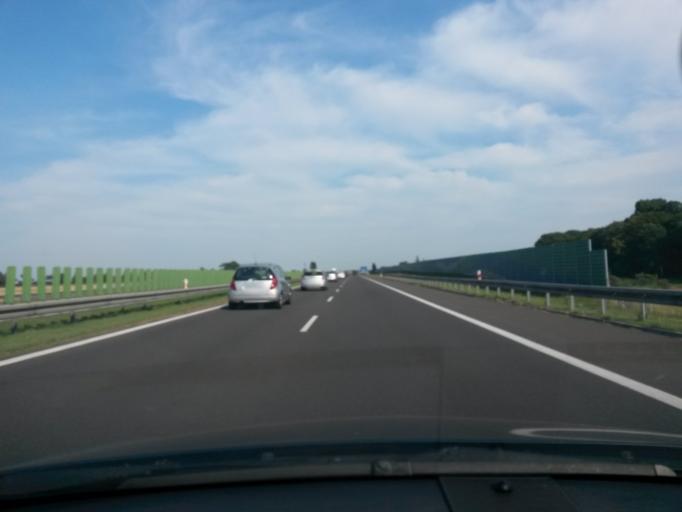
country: PL
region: Greater Poland Voivodeship
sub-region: Powiat slupecki
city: Strzalkowo
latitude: 52.2608
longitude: 17.7826
